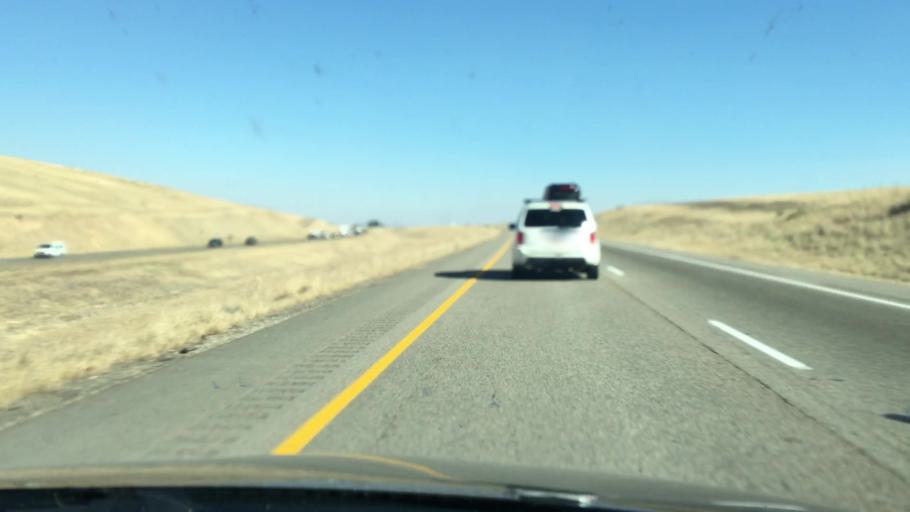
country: US
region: Idaho
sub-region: Ada County
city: Boise
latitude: 43.4897
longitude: -116.1245
